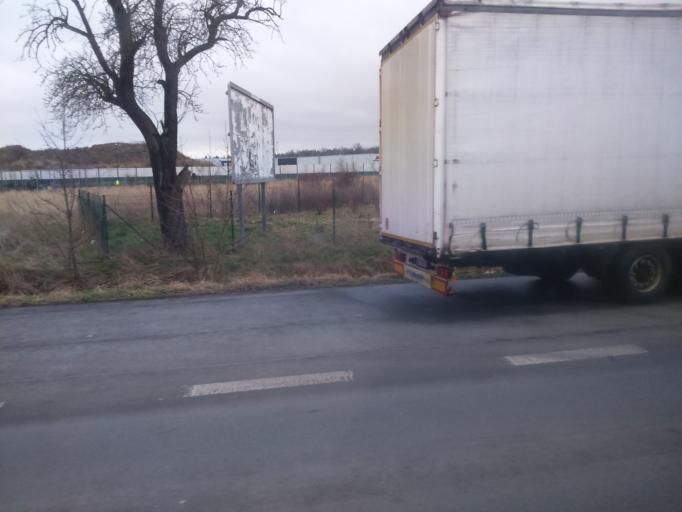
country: CZ
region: Plzensky
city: Vejprnice
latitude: 49.7299
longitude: 13.3137
